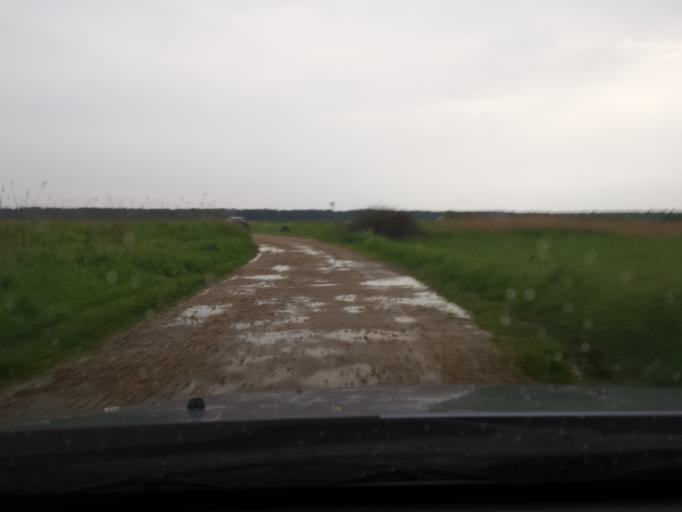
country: LV
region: Riga
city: Bolderaja
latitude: 57.0554
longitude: 24.0952
